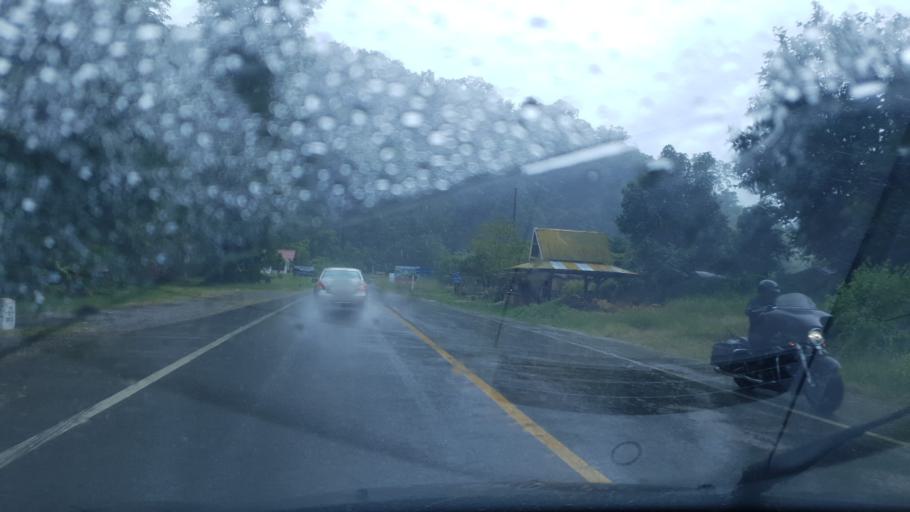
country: TH
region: Mae Hong Son
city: Khun Yuam
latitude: 18.6491
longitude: 97.9397
